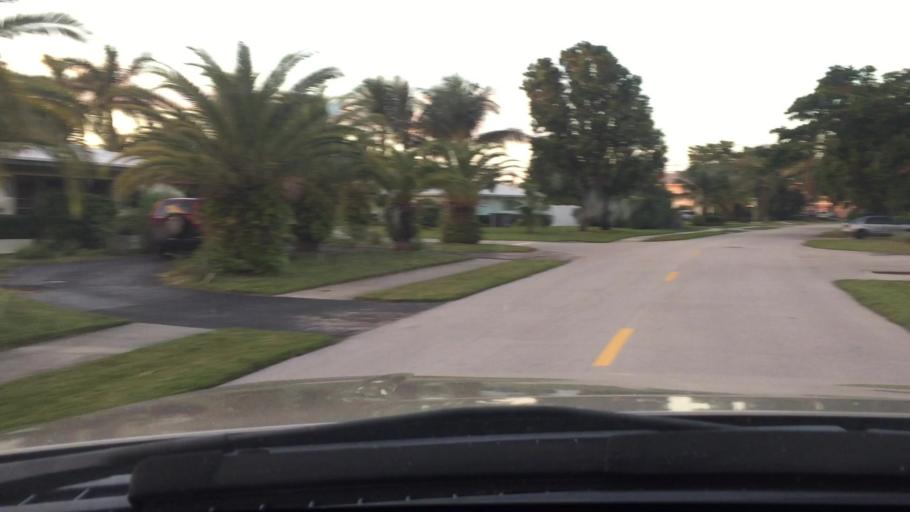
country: US
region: Florida
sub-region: Broward County
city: Deerfield Beach
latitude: 26.3118
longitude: -80.0851
